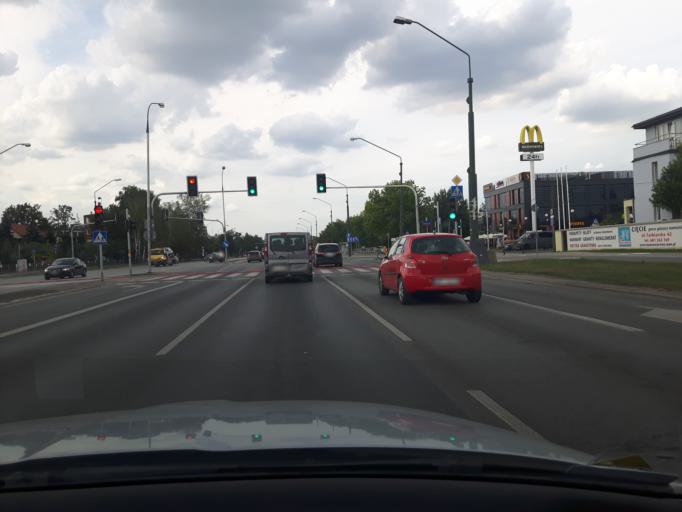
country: PL
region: Masovian Voivodeship
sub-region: Powiat piaseczynski
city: Mysiadlo
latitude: 52.1227
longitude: 21.0184
